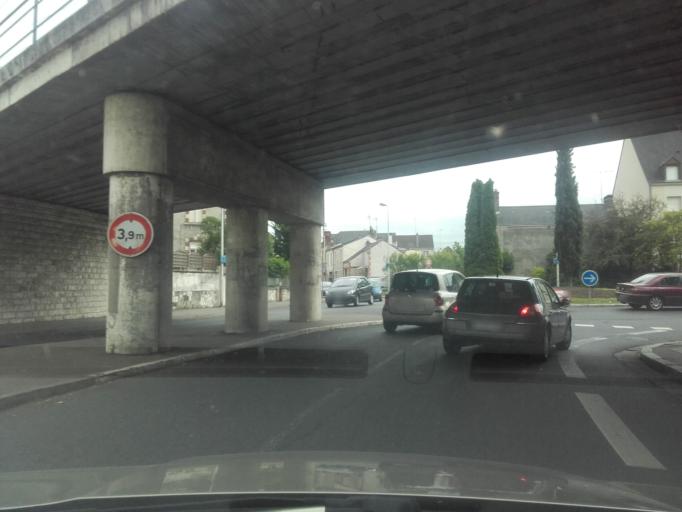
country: FR
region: Centre
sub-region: Departement d'Indre-et-Loire
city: Tours
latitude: 47.3817
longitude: 0.7065
